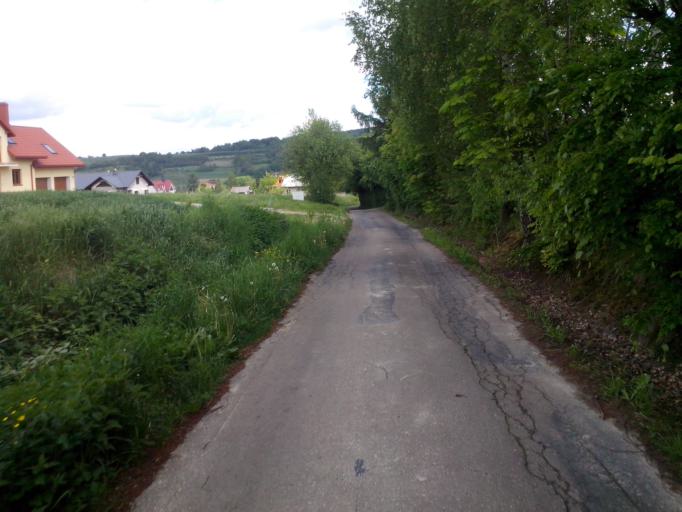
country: PL
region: Subcarpathian Voivodeship
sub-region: Powiat strzyzowski
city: Strzyzow
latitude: 49.8389
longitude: 21.8095
